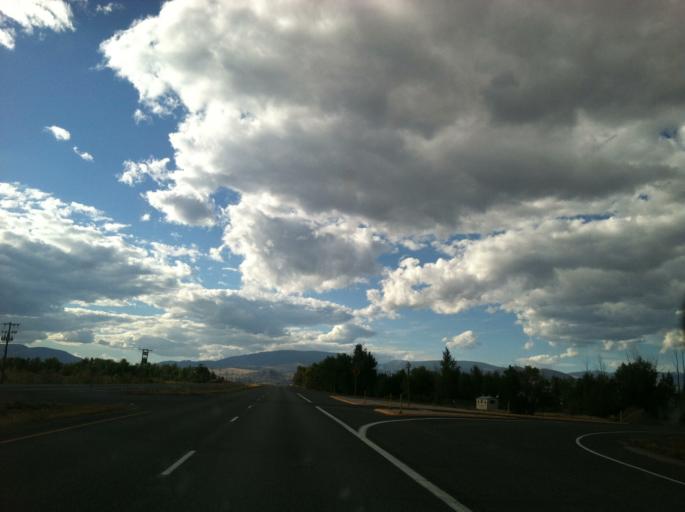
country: US
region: Montana
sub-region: Deer Lodge County
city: Anaconda
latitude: 46.1068
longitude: -112.8479
